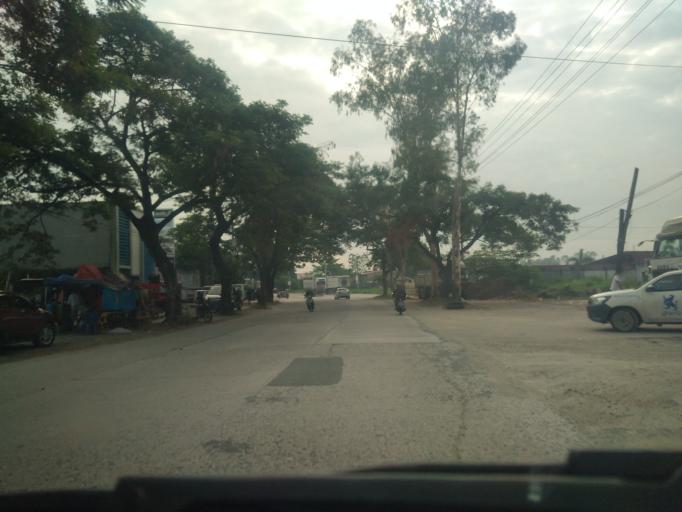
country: PH
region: Central Luzon
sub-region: Province of Pampanga
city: Calibutbut
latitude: 15.1158
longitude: 120.5952
